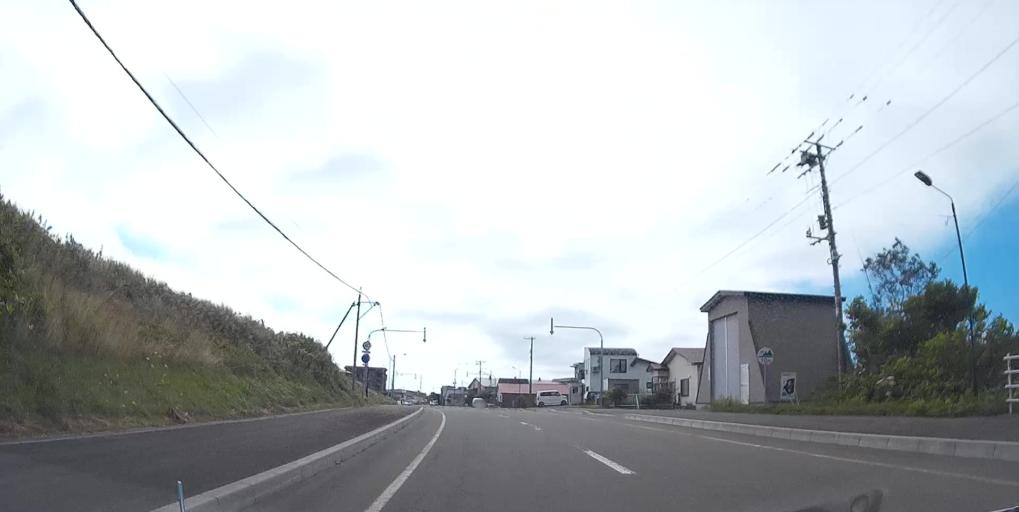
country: JP
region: Hokkaido
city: Kamiiso
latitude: 41.9714
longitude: 140.1450
